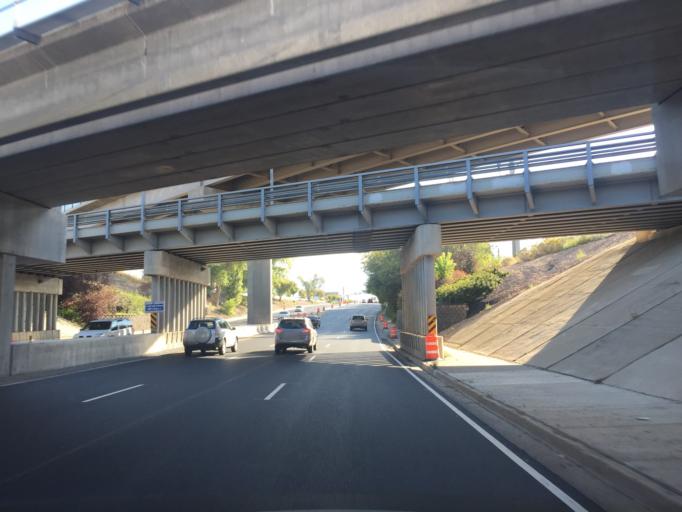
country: US
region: Utah
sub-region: Salt Lake County
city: Murray
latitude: 40.6551
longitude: -111.8983
